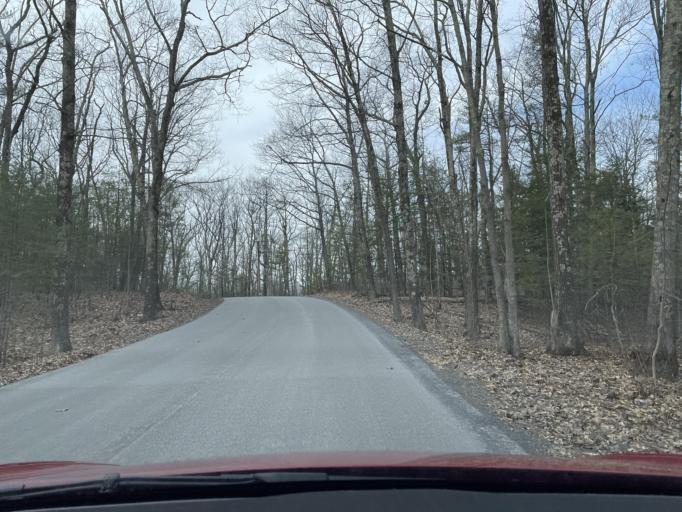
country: US
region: New York
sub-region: Ulster County
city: Saugerties
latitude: 42.1093
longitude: -73.9868
